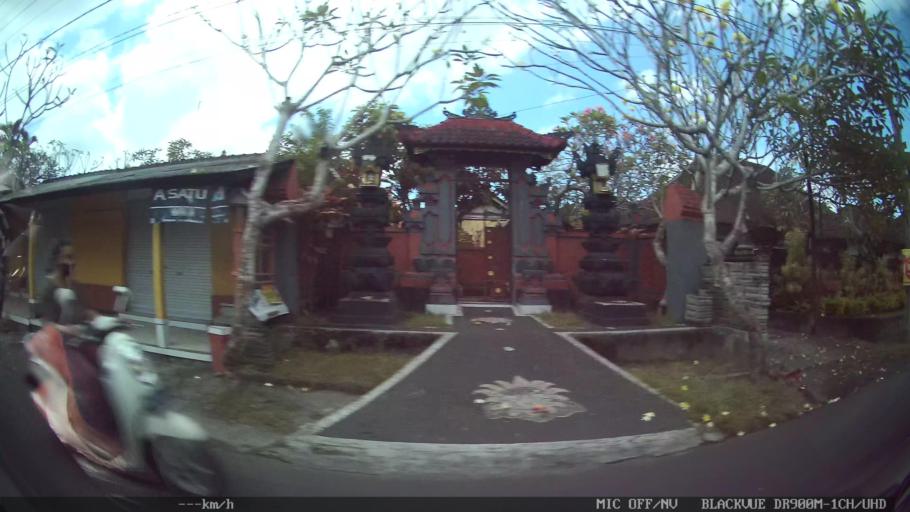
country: ID
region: Bali
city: Banjar Sedang
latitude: -8.5621
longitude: 115.2863
